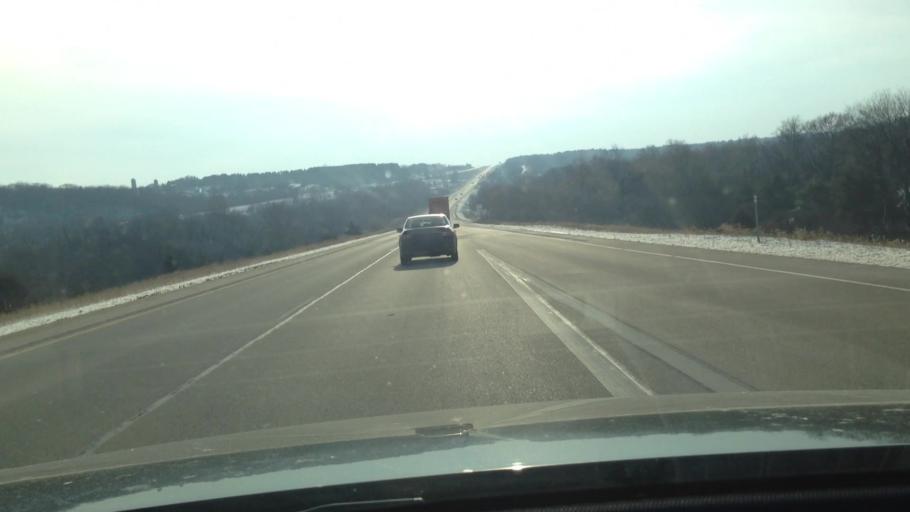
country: US
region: Wisconsin
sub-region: Walworth County
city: East Troy
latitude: 42.7290
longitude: -88.4634
